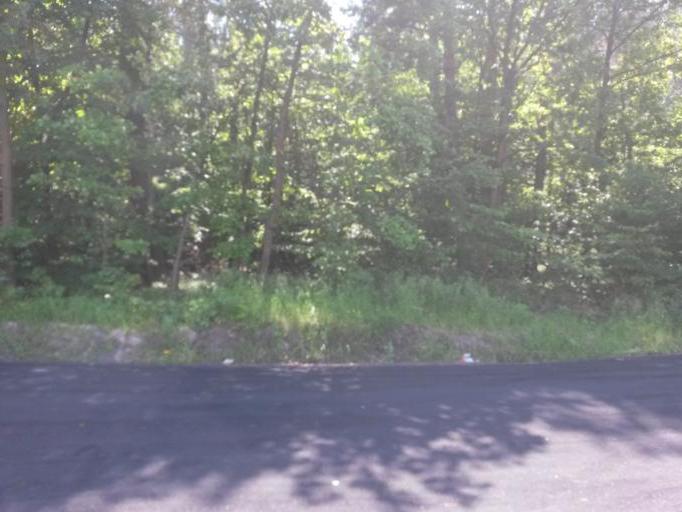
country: PL
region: Lublin Voivodeship
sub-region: Powiat radzynski
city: Borki
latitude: 51.7507
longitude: 22.5510
